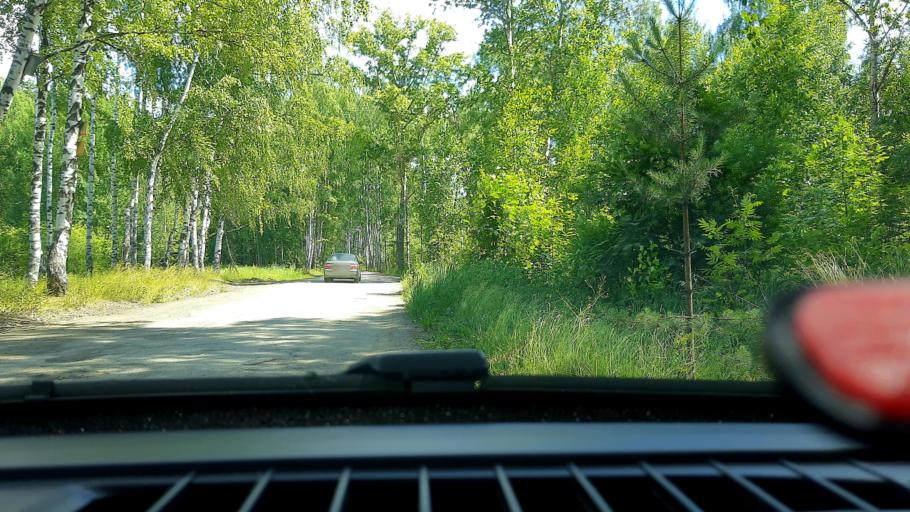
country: RU
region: Nizjnij Novgorod
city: Gorbatovka
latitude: 56.2955
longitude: 43.8166
